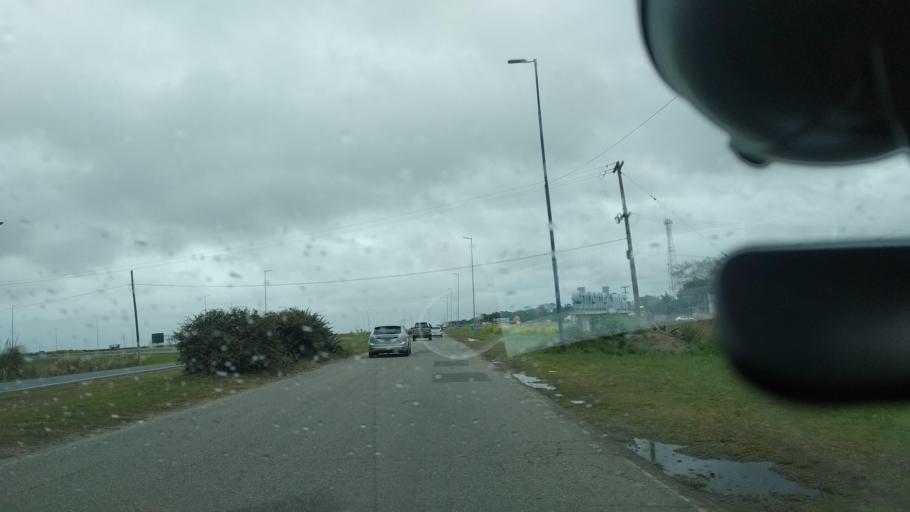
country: AR
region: Buenos Aires
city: San Clemente del Tuyu
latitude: -36.3880
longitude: -56.7368
